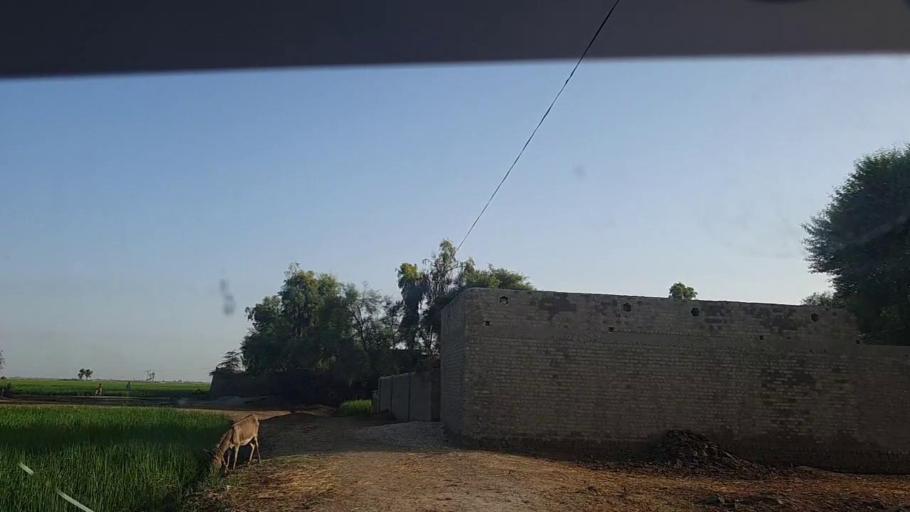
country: PK
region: Sindh
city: Thul
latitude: 28.2107
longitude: 68.8860
